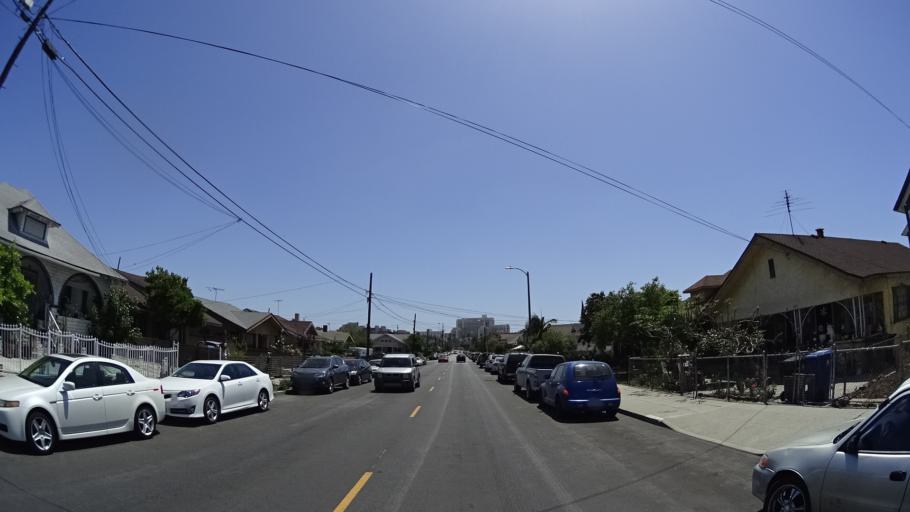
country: US
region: California
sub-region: Los Angeles County
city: Boyle Heights
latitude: 34.0698
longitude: -118.2079
